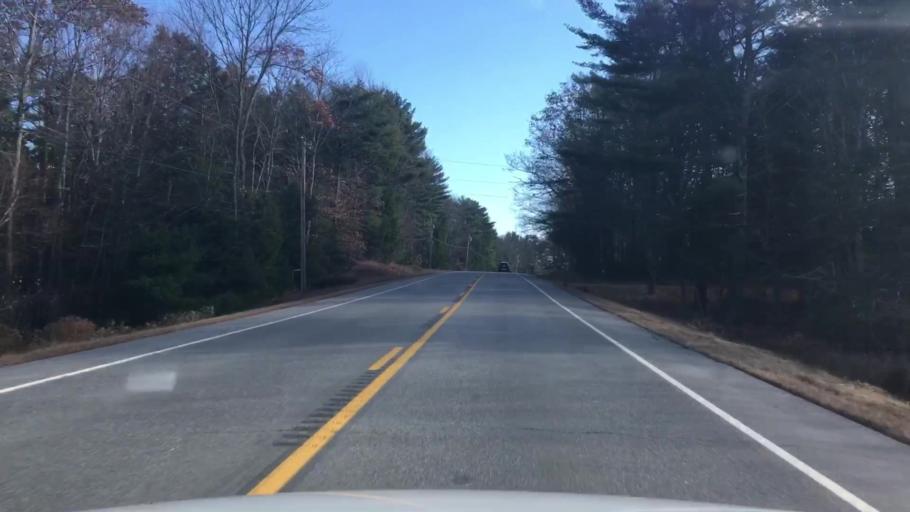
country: US
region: Maine
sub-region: Lincoln County
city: Jefferson
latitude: 44.2590
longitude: -69.4511
